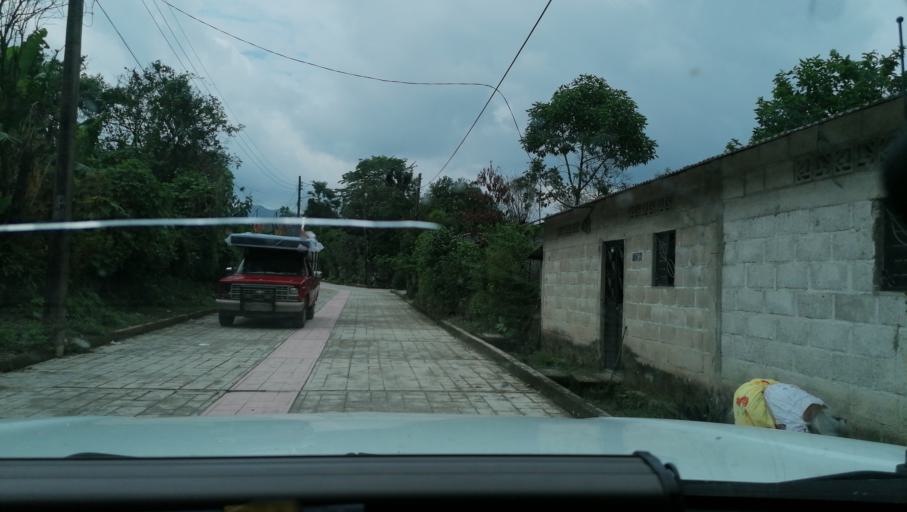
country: MX
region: Chiapas
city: Ixtacomitan
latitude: 17.3369
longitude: -93.1291
